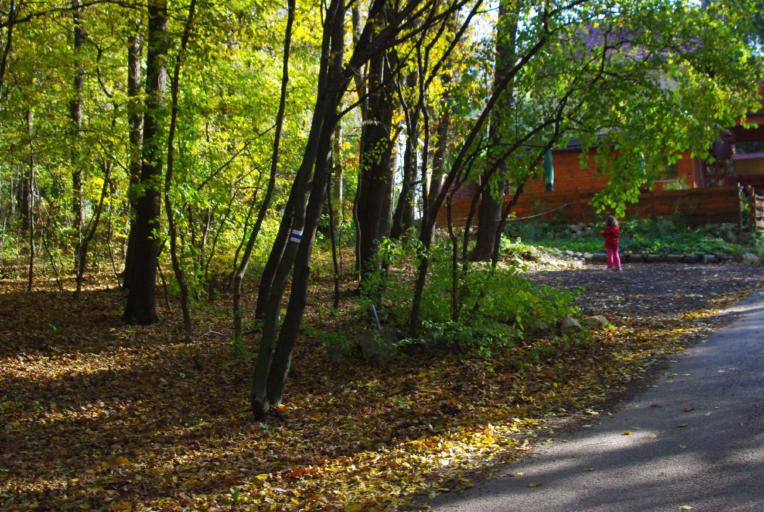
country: HU
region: Komarom-Esztergom
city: Piliscsev
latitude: 47.7021
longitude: 18.8326
